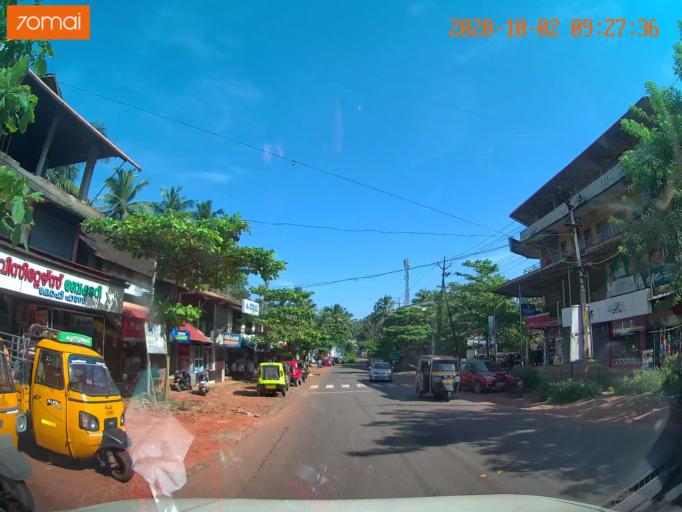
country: IN
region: Kerala
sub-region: Kozhikode
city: Naduvannur
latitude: 11.5996
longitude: 75.7649
